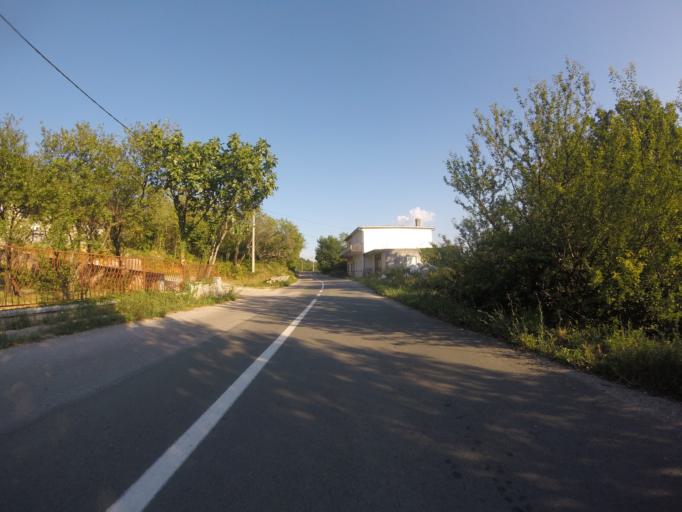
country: HR
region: Primorsko-Goranska
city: Selce
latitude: 45.1795
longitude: 14.7384
